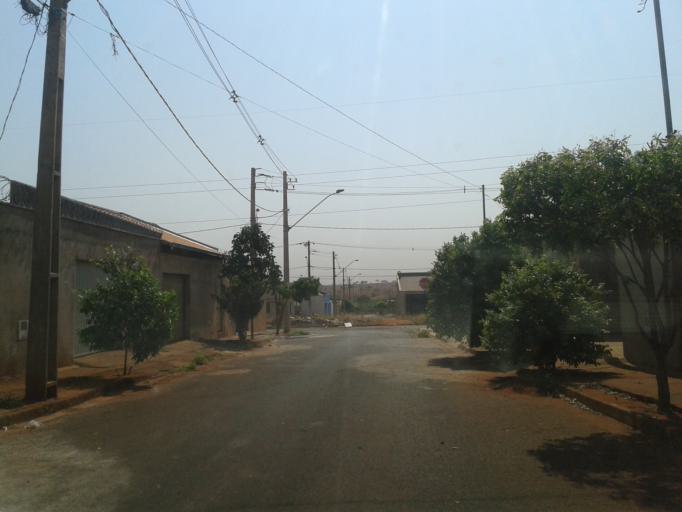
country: BR
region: Minas Gerais
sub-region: Ituiutaba
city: Ituiutaba
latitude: -18.9864
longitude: -49.4265
